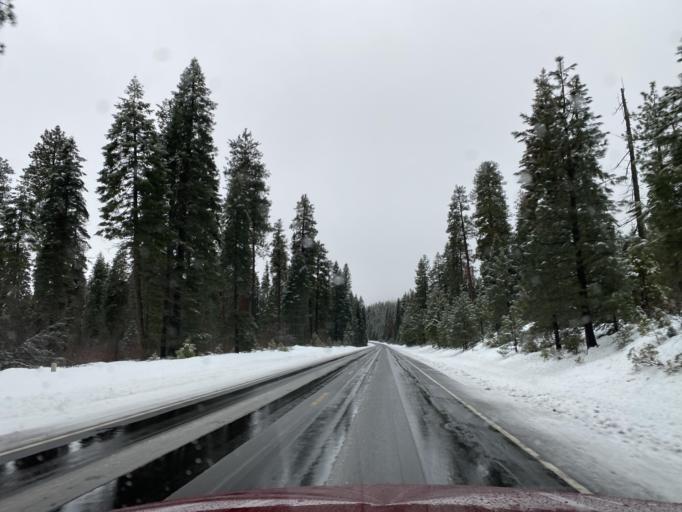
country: US
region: Oregon
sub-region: Klamath County
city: Klamath Falls
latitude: 42.5429
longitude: -122.0884
